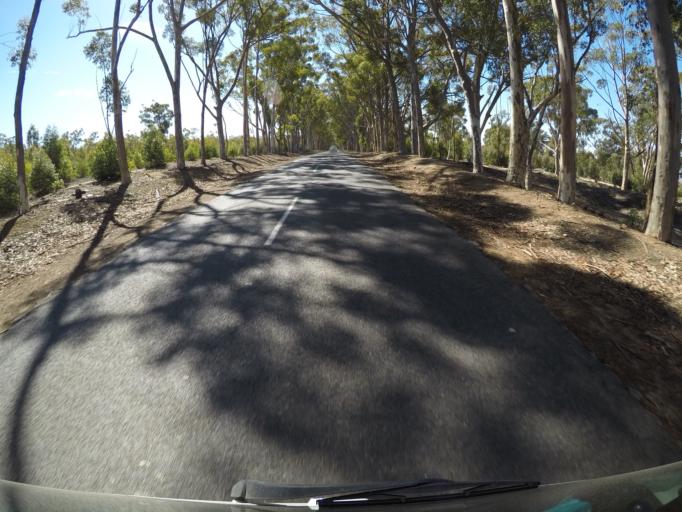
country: ZA
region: Western Cape
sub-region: City of Cape Town
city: Sunset Beach
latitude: -33.7549
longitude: 18.5548
